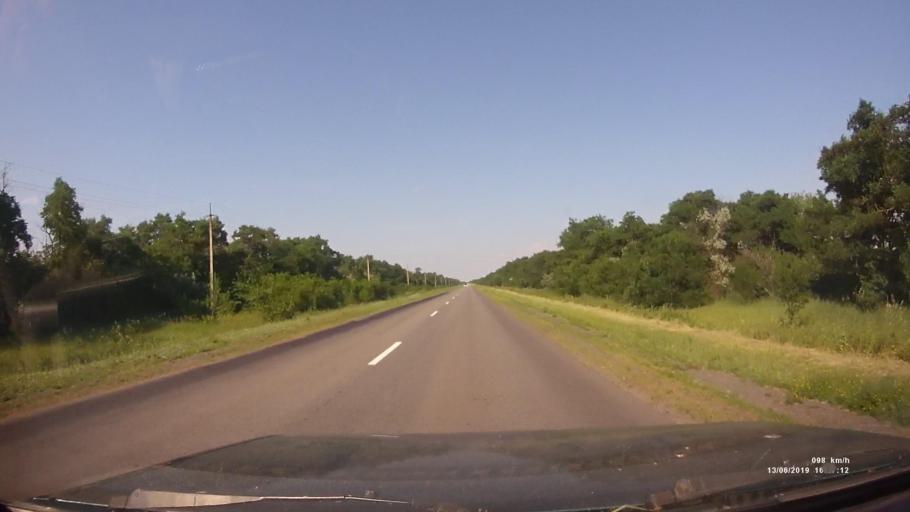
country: RU
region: Rostov
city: Kazanskaya
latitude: 49.8113
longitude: 41.1787
